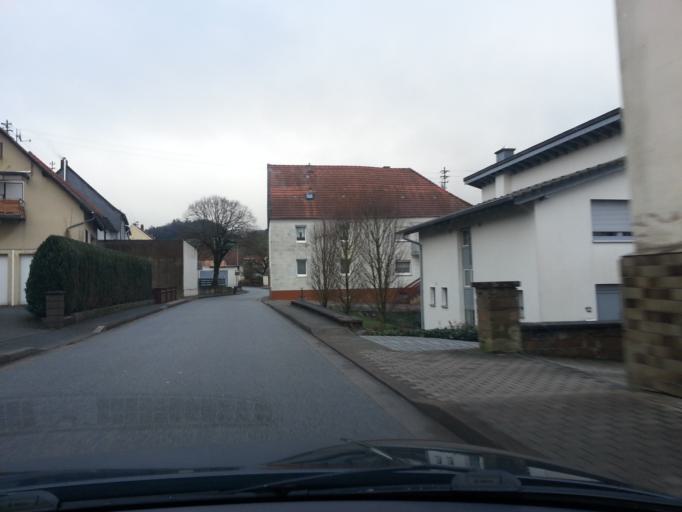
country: DE
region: Rheinland-Pfalz
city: Herchweiler
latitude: 49.5139
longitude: 7.2918
